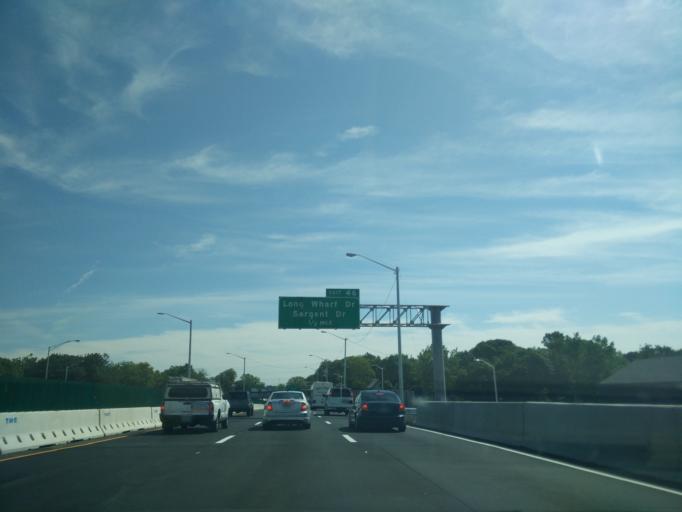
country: US
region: Connecticut
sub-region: New Haven County
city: West Haven
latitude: 41.2838
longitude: -72.9345
